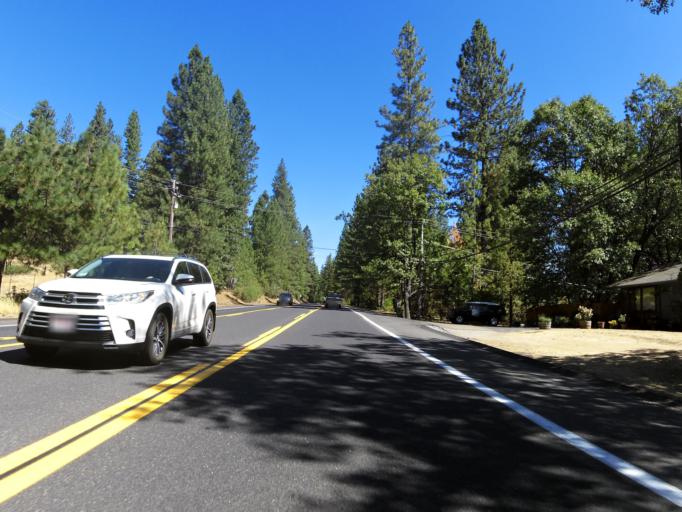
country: US
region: California
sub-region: Calaveras County
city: Arnold
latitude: 38.2062
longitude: -120.3691
